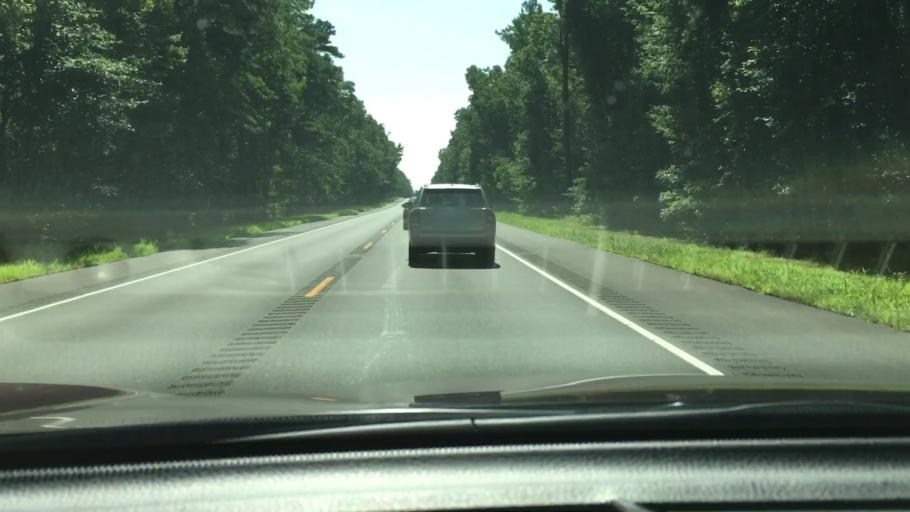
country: US
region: New Jersey
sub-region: Cape May County
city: Woodbine
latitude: 39.3322
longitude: -74.8785
